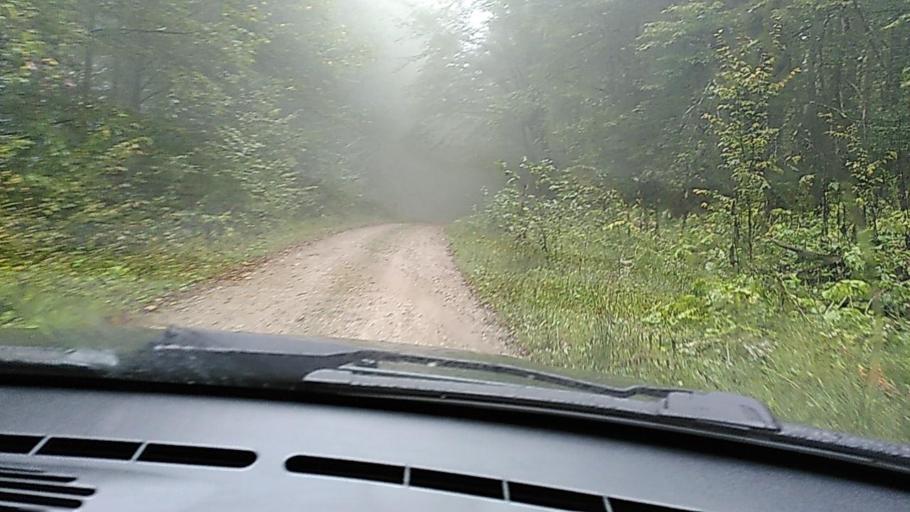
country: RU
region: Kabardino-Balkariya
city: Belaya Rechka
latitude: 43.3695
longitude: 43.4235
